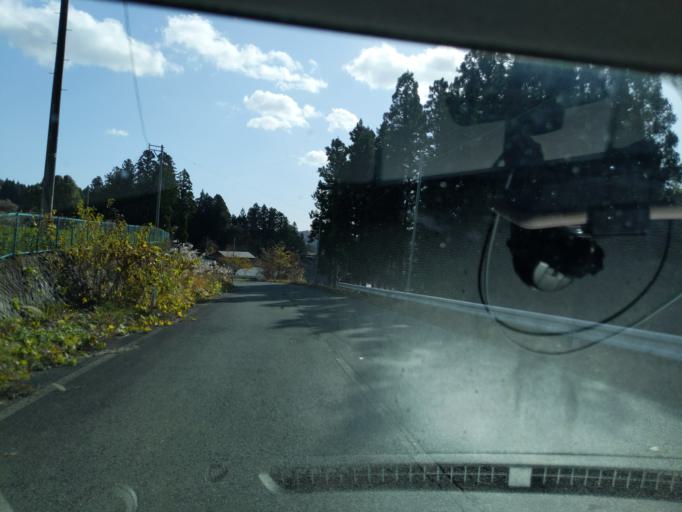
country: JP
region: Iwate
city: Mizusawa
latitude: 39.0349
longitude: 141.0780
